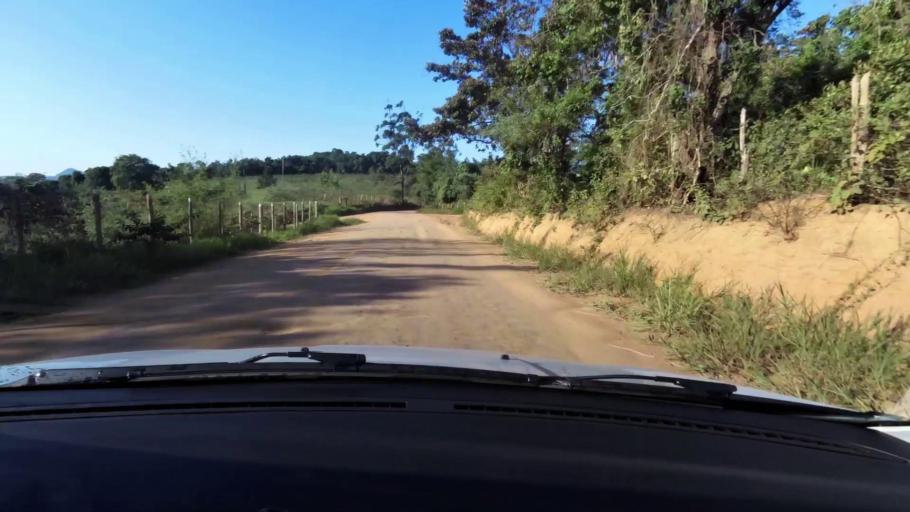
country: BR
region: Espirito Santo
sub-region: Guarapari
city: Guarapari
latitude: -20.7243
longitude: -40.5871
